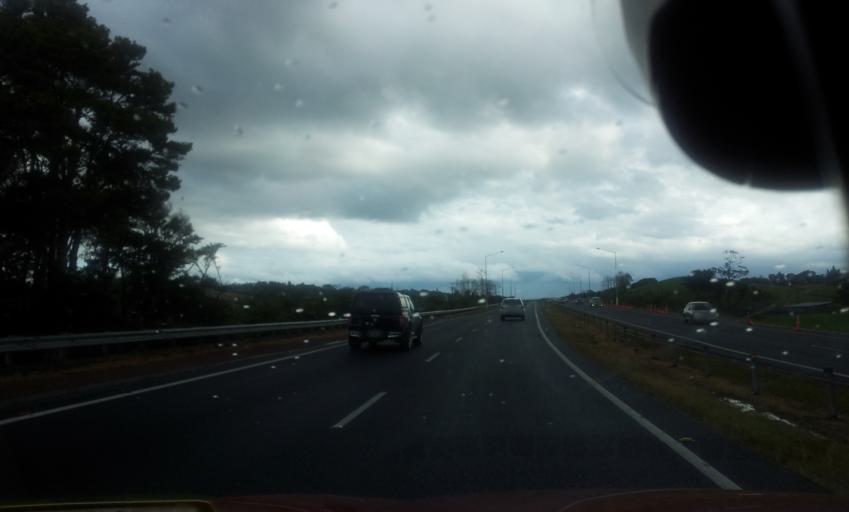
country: NZ
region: Auckland
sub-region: Auckland
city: Rothesay Bay
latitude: -36.6176
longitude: 174.6630
